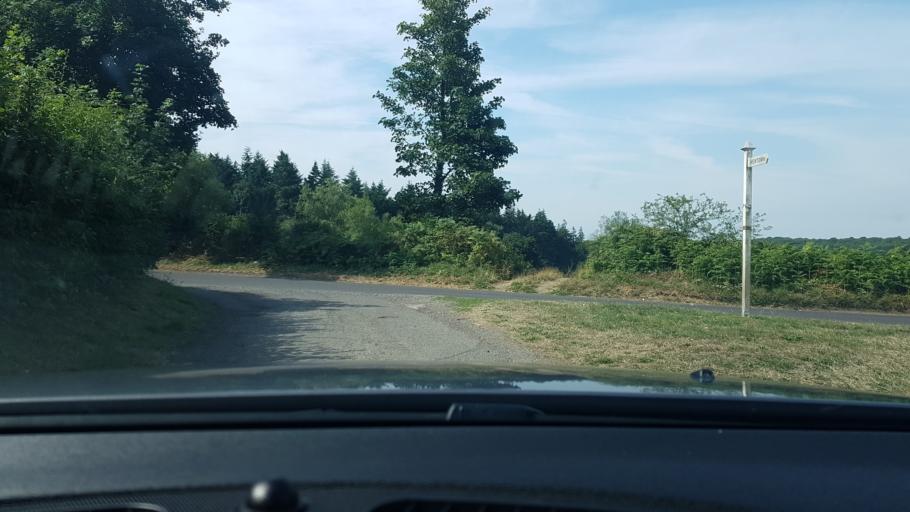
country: GB
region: England
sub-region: Wiltshire
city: Shalbourne
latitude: 51.3659
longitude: -1.5723
